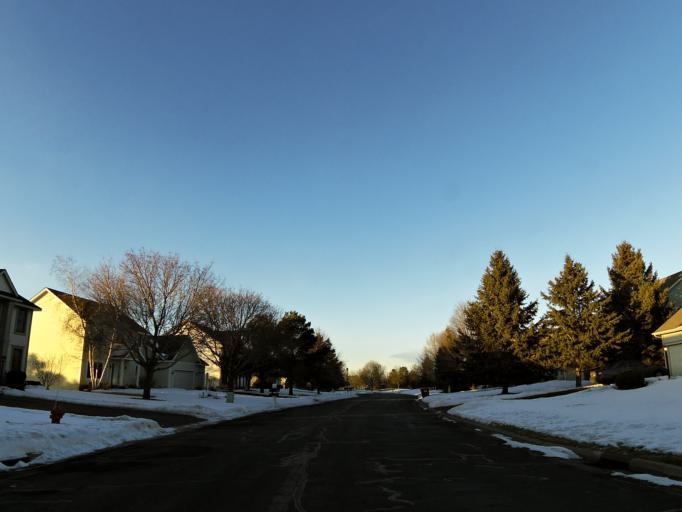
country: US
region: Minnesota
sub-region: Washington County
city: Woodbury
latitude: 44.8929
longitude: -92.8996
